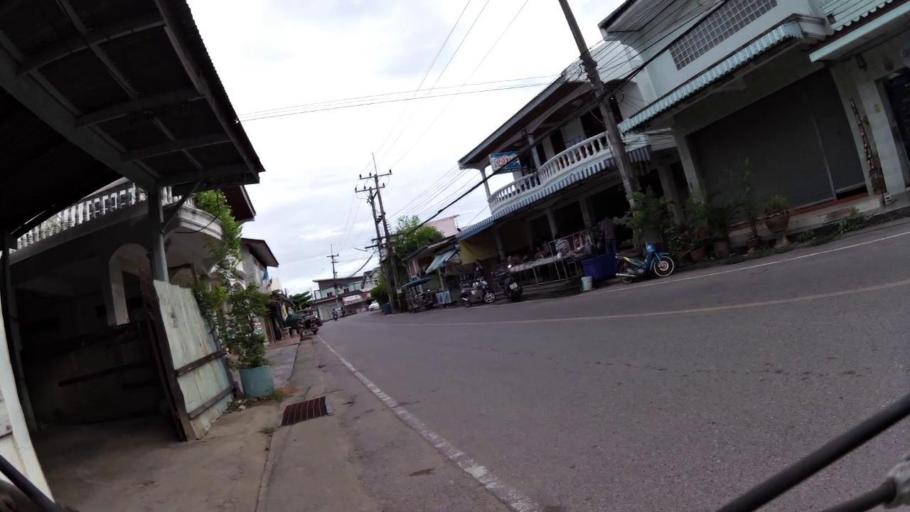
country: TH
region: Prachuap Khiri Khan
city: Prachuap Khiri Khan
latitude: 11.7467
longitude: 99.7901
